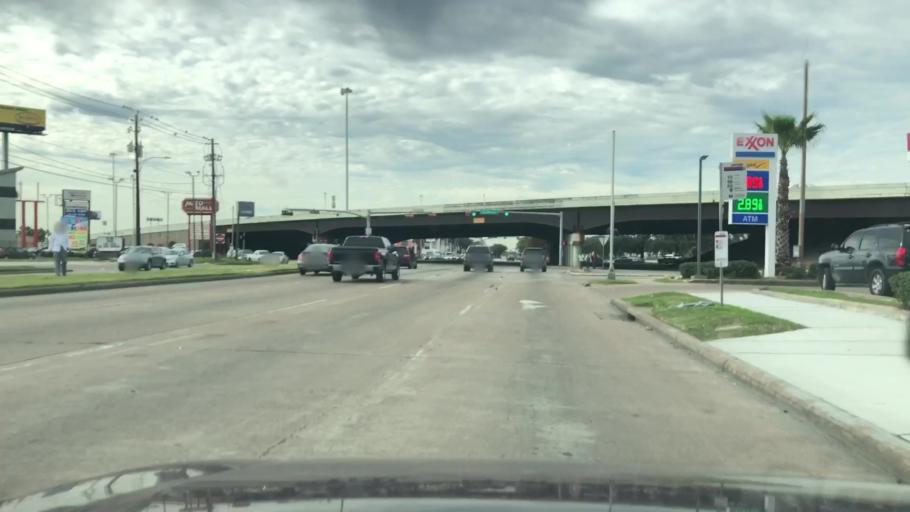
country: US
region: Texas
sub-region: Fort Bend County
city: Meadows Place
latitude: 29.6762
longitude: -95.5404
